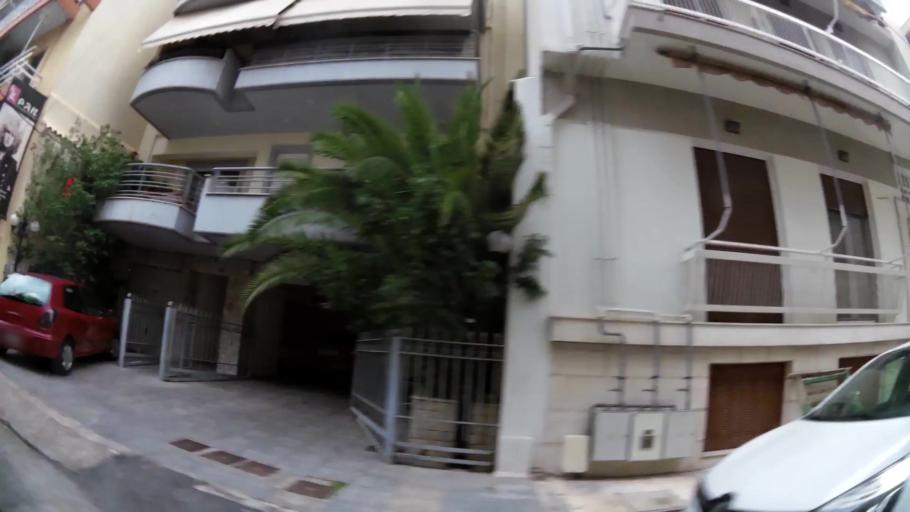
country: GR
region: Attica
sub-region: Nomos Attikis
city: Piraeus
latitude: 37.9554
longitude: 23.6418
